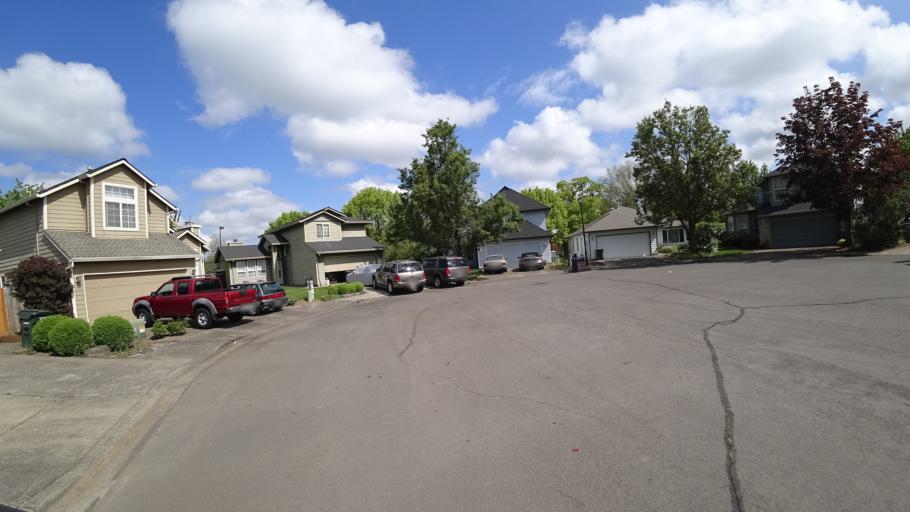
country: US
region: Oregon
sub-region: Washington County
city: Aloha
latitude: 45.5111
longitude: -122.8900
